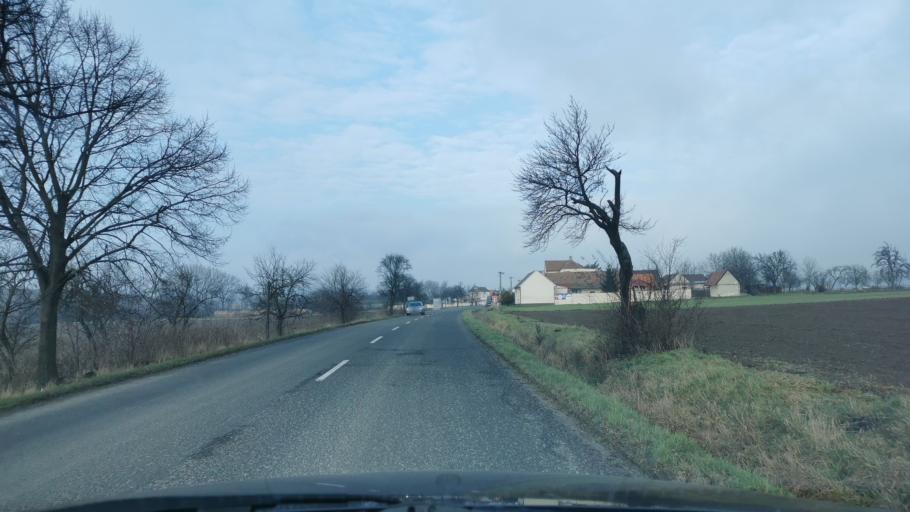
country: SK
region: Trnavsky
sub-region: Okres Senica
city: Senica
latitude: 48.7013
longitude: 17.3441
